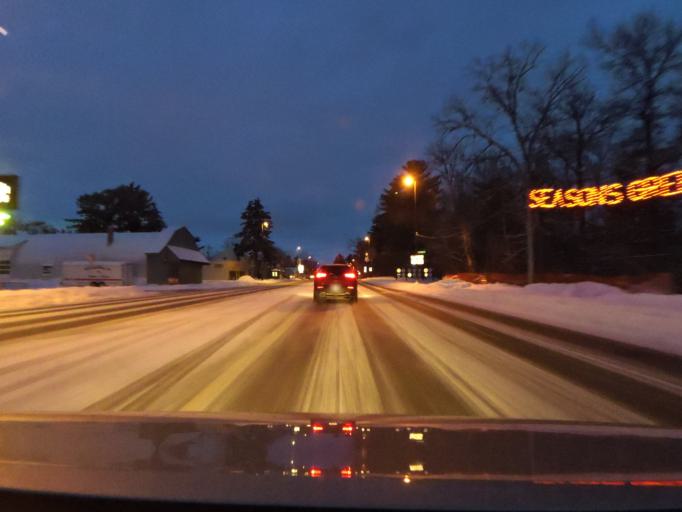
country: US
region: Wisconsin
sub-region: Dunn County
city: Menomonie
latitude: 44.8955
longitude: -91.9322
